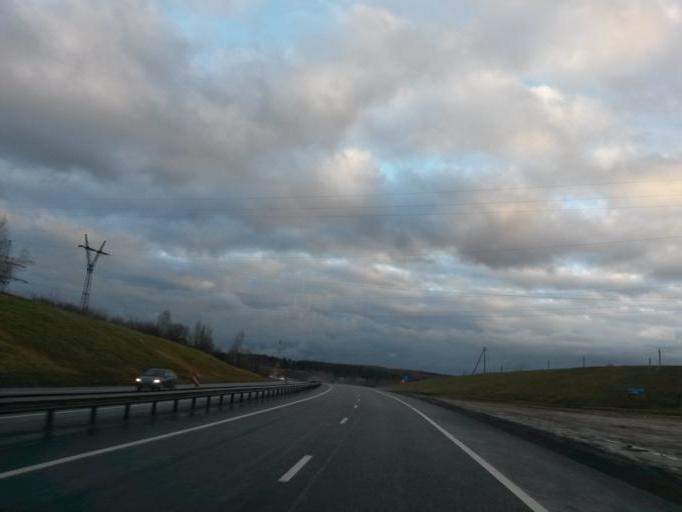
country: RU
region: Moskovskaya
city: Svatkovo
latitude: 56.3808
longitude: 38.3235
